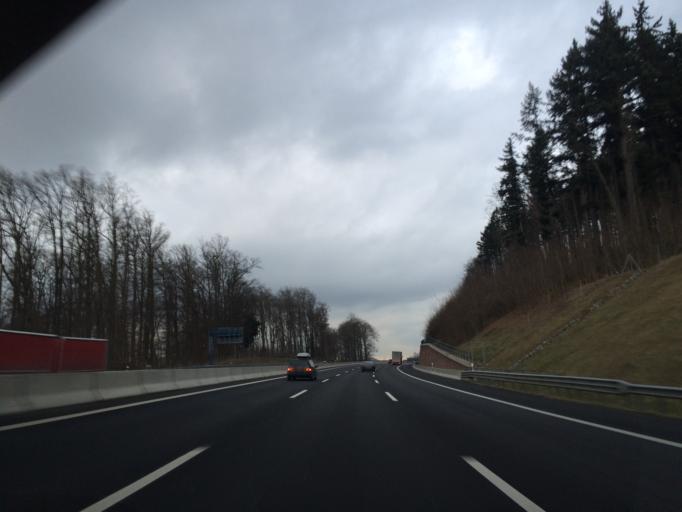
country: DE
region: Bavaria
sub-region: Regierungsbezirk Unterfranken
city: Sailauf
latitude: 49.9877
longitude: 9.2567
